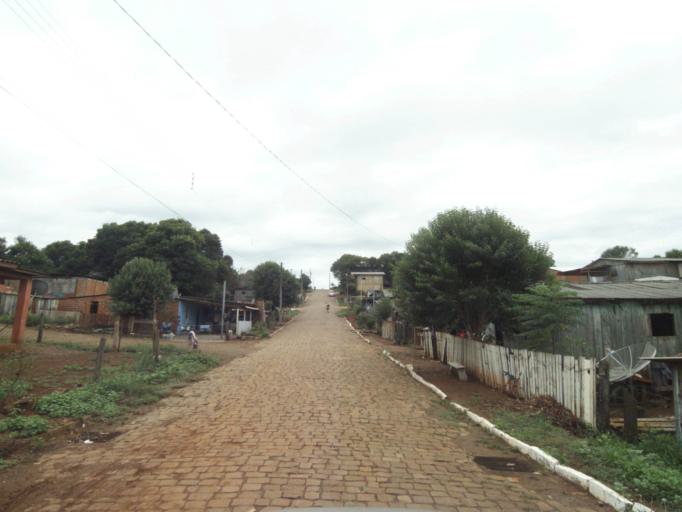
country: BR
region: Rio Grande do Sul
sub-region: Lagoa Vermelha
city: Lagoa Vermelha
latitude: -28.2253
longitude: -51.5402
